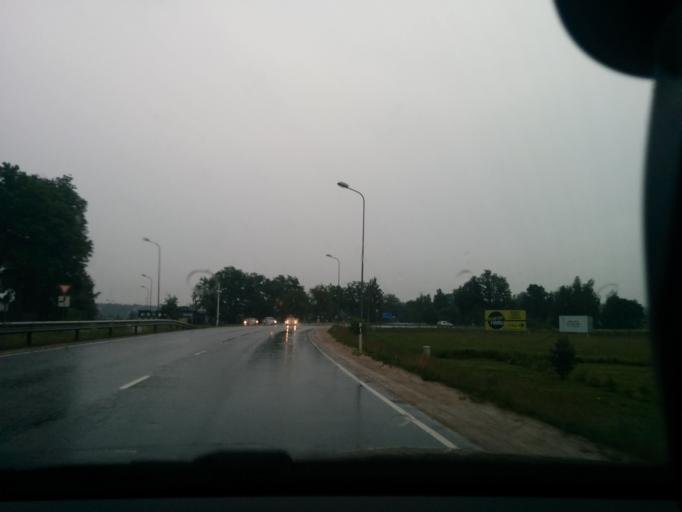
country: LV
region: Ikskile
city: Ikskile
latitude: 56.8655
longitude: 24.5584
